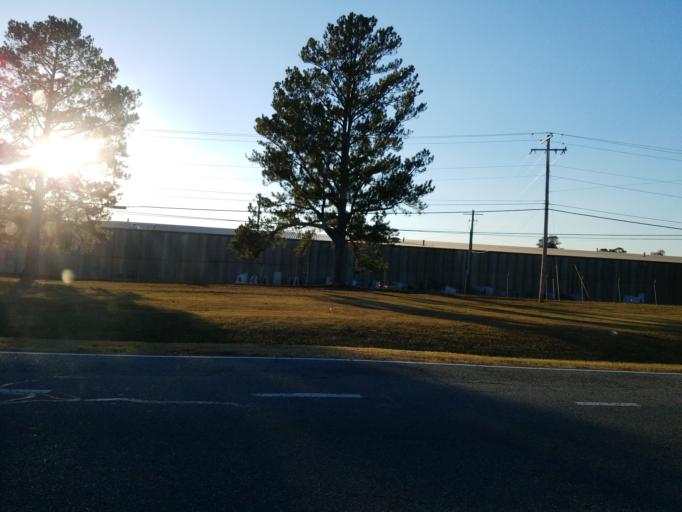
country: US
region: Georgia
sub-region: Gordon County
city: Calhoun
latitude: 34.4709
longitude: -84.9344
